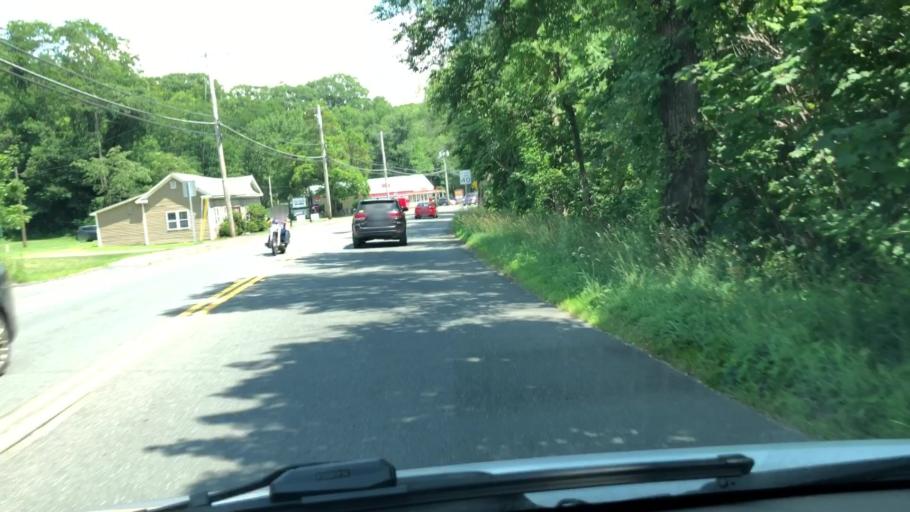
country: US
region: Massachusetts
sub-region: Hampshire County
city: Williamsburg
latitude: 42.3907
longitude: -72.7232
